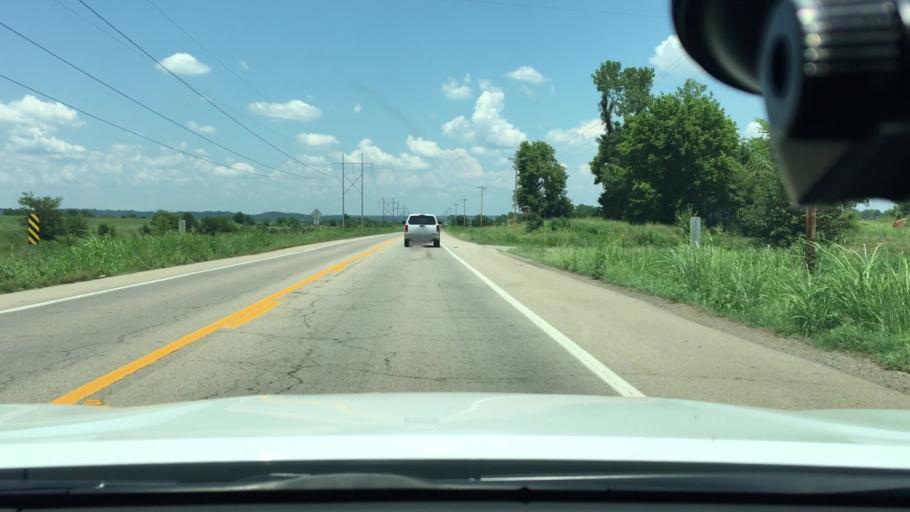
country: US
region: Arkansas
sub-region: Crawford County
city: Van Buren
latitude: 35.3945
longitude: -94.3304
